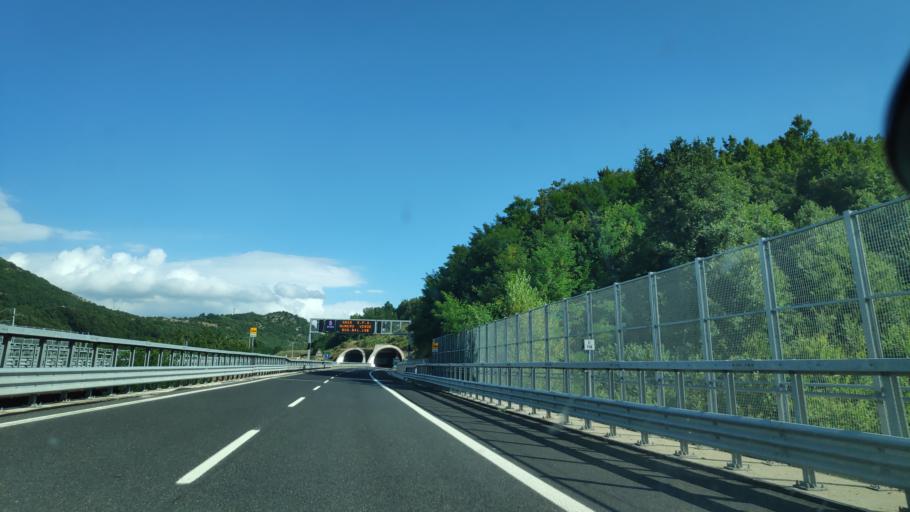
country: IT
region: Campania
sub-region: Provincia di Salerno
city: Casalbuono
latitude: 40.2301
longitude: 15.6678
